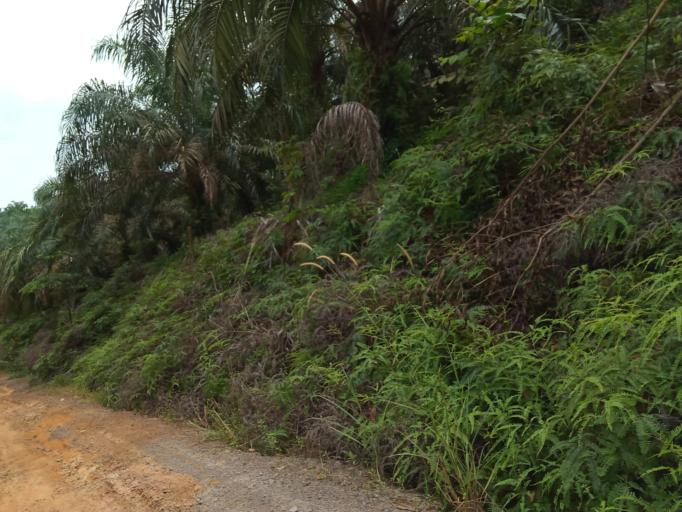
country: ID
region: Jambi
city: Muara Bulian
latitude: -1.5589
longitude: 103.2356
